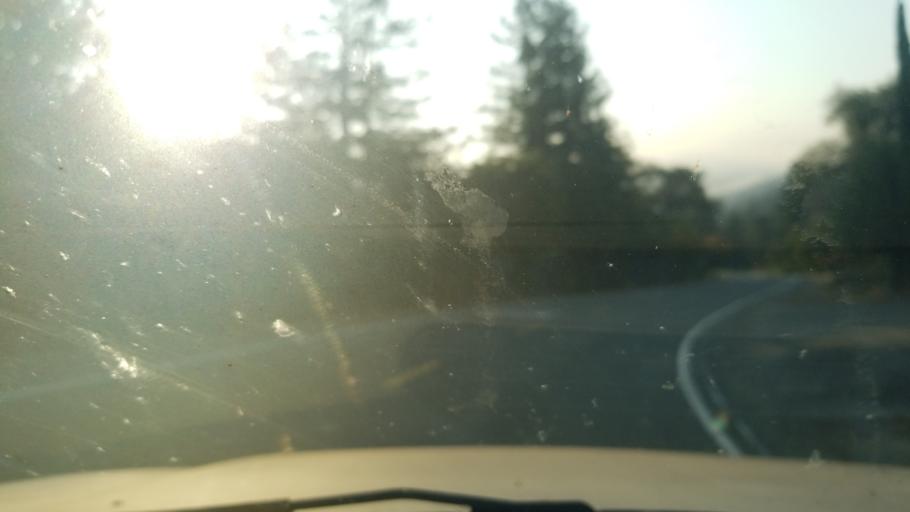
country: US
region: California
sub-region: Humboldt County
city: Redway
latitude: 40.0670
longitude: -123.7889
